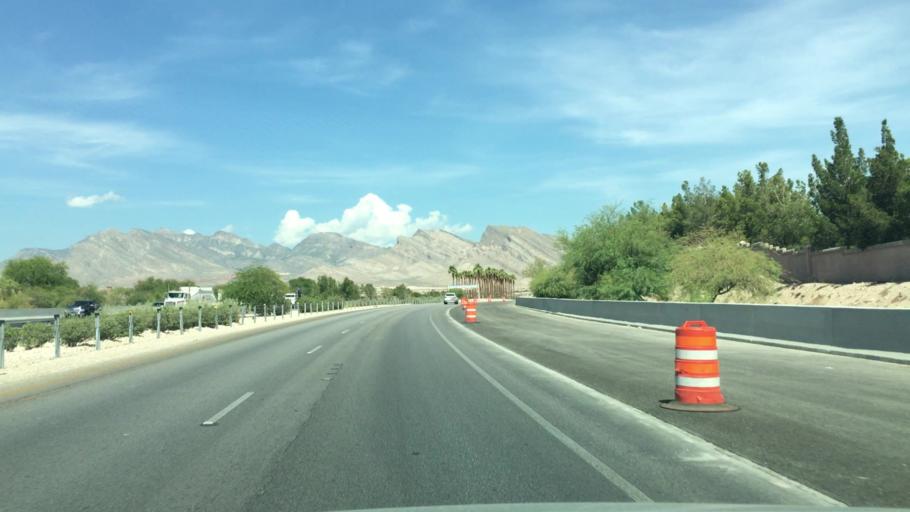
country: US
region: Nevada
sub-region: Clark County
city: Summerlin South
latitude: 36.1792
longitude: -115.2953
